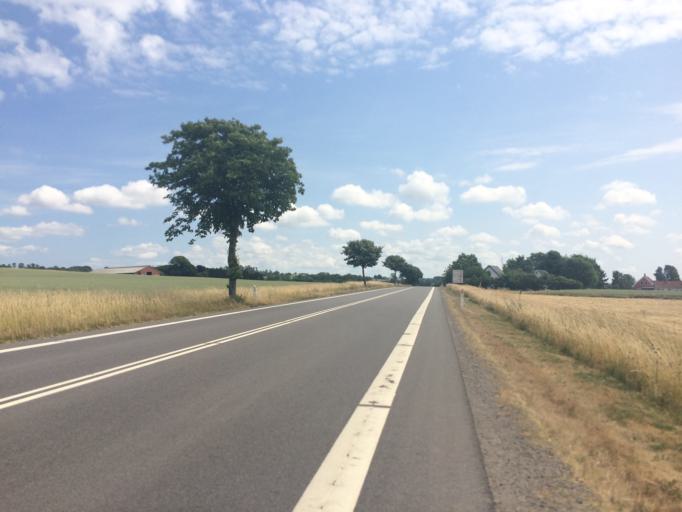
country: DK
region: Capital Region
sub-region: Bornholm Kommune
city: Ronne
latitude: 55.1799
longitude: 14.7235
